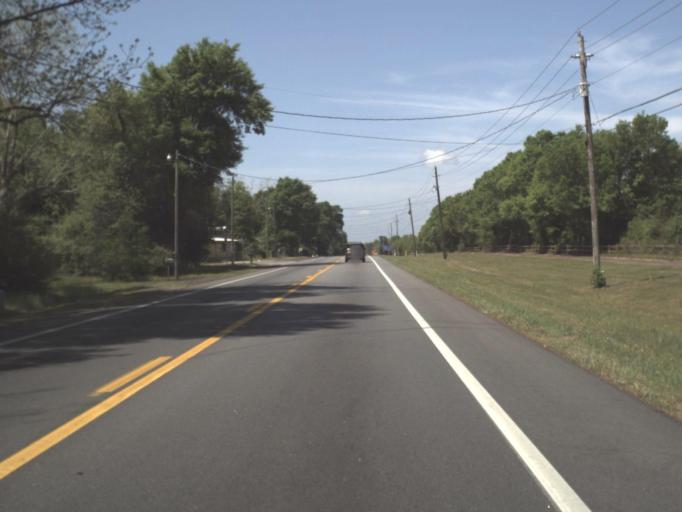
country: US
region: Florida
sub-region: Santa Rosa County
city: East Milton
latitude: 30.6275
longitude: -87.0057
